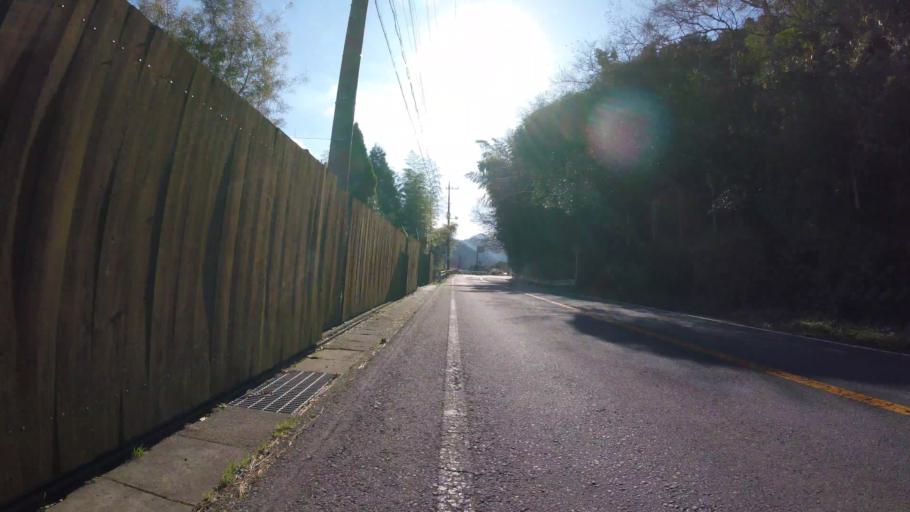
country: JP
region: Shizuoka
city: Ito
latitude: 34.9374
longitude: 139.0618
